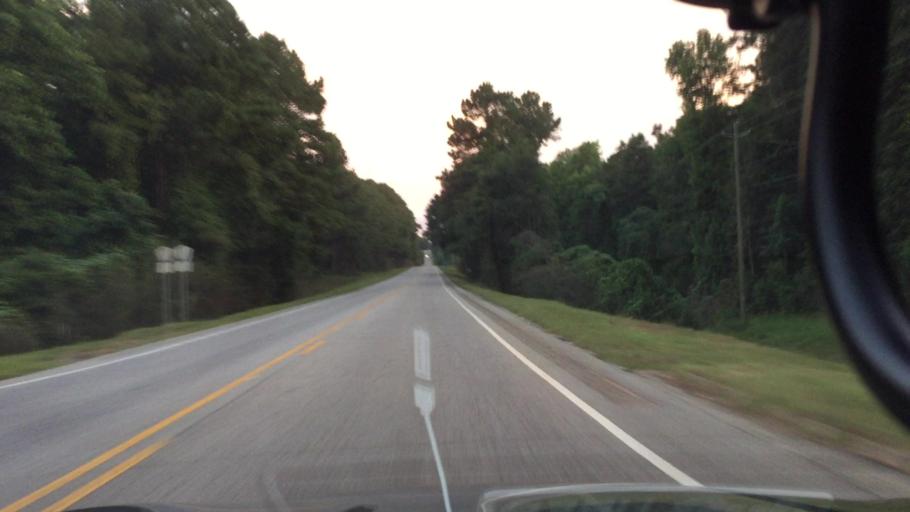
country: US
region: Alabama
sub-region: Coffee County
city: New Brockton
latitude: 31.3916
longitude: -85.8775
